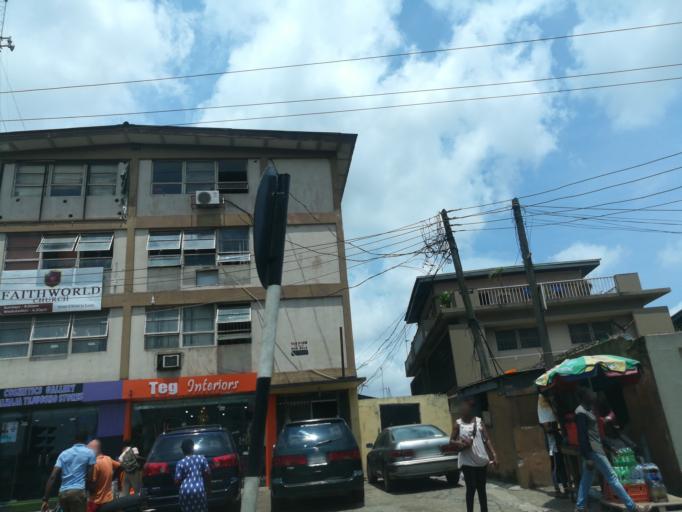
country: NG
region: Lagos
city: Somolu
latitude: 6.5464
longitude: 3.3620
